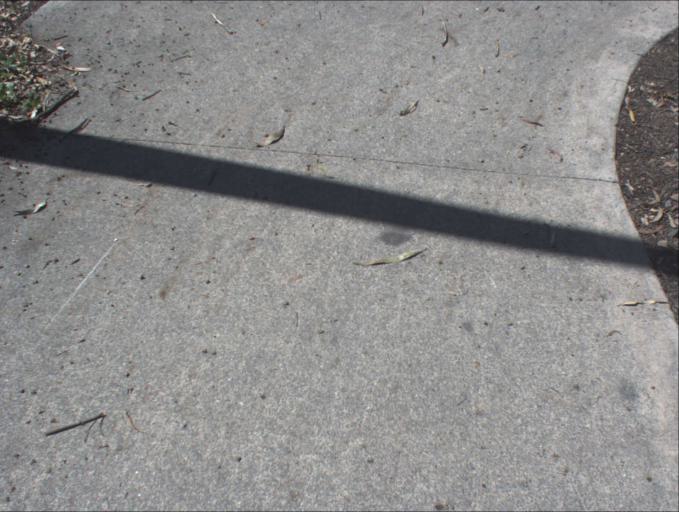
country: AU
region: Queensland
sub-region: Logan
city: Waterford West
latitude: -27.7155
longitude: 153.1461
